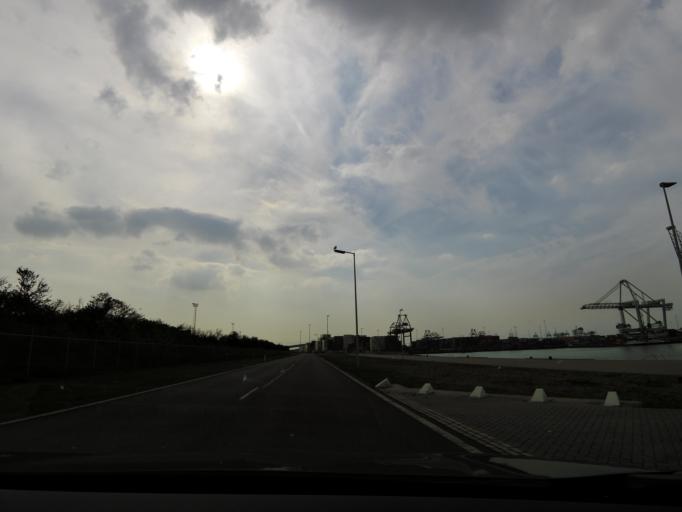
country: NL
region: South Holland
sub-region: Gemeente Rotterdam
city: Hoek van Holland
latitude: 51.9441
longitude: 4.0463
